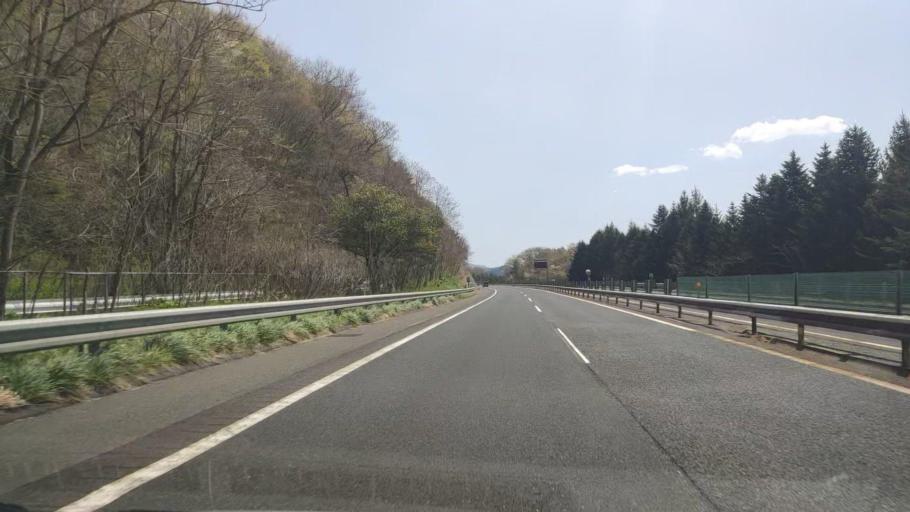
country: JP
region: Iwate
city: Ichinohe
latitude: 40.2321
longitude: 141.3030
